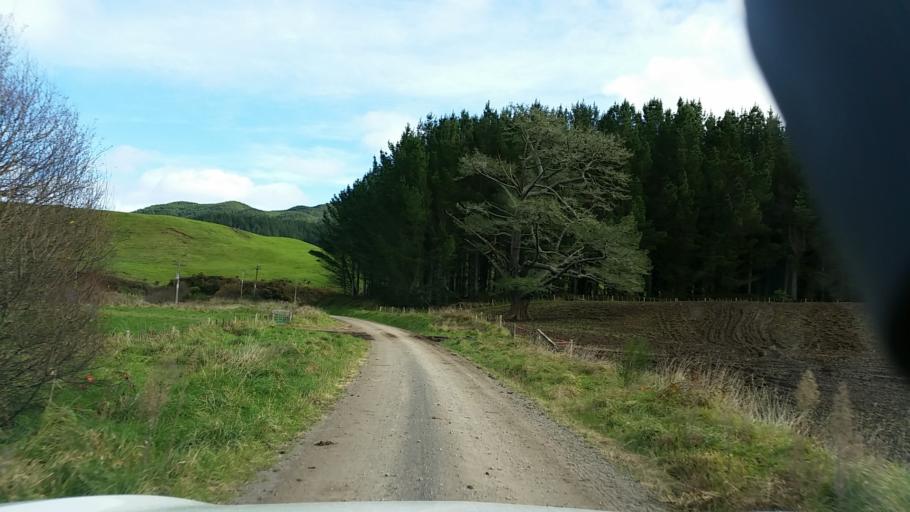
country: NZ
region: Bay of Plenty
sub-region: Rotorua District
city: Rotorua
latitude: -38.2375
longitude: 176.2242
